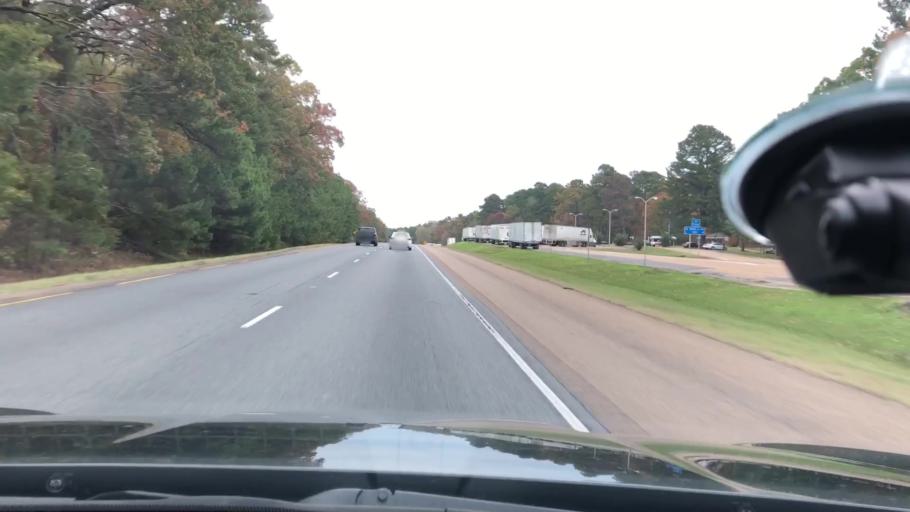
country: US
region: Arkansas
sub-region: Clark County
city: Gurdon
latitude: 33.9286
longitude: -93.2620
